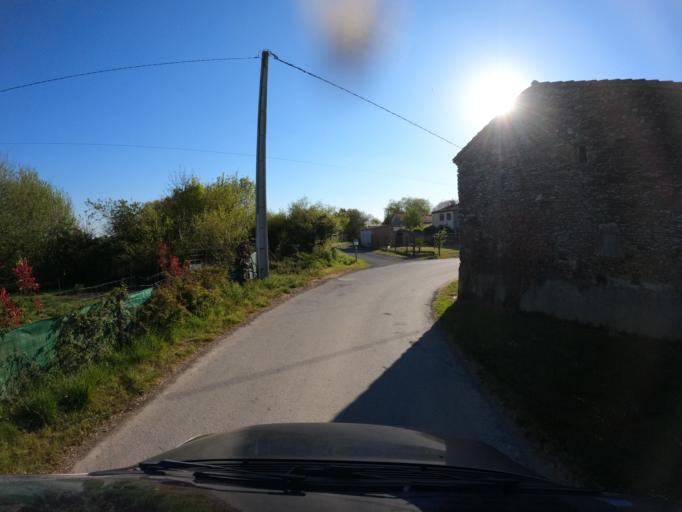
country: FR
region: Pays de la Loire
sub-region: Departement de la Vendee
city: Les Brouzils
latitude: 46.8896
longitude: -1.3471
